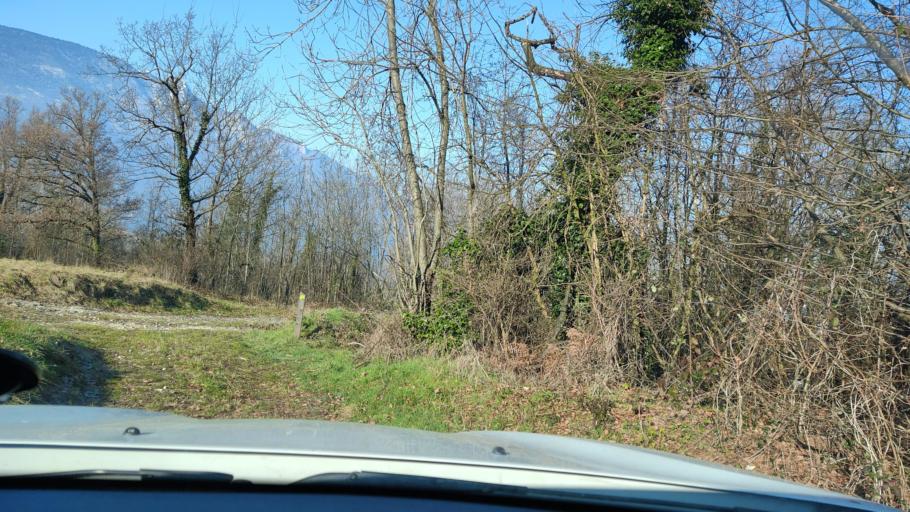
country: FR
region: Rhone-Alpes
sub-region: Departement de la Savoie
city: Voglans
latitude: 45.6399
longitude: 5.9017
